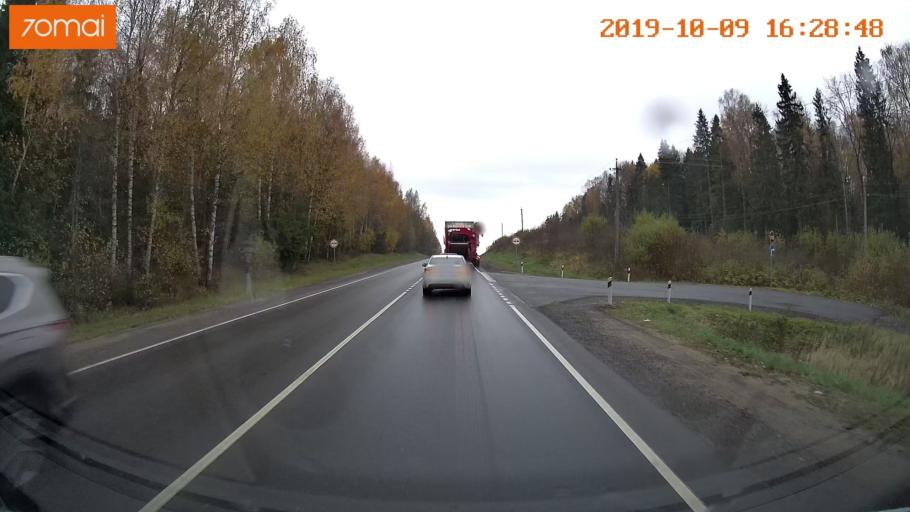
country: RU
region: Kostroma
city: Oktyabr'skiy
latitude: 57.6269
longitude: 40.9336
